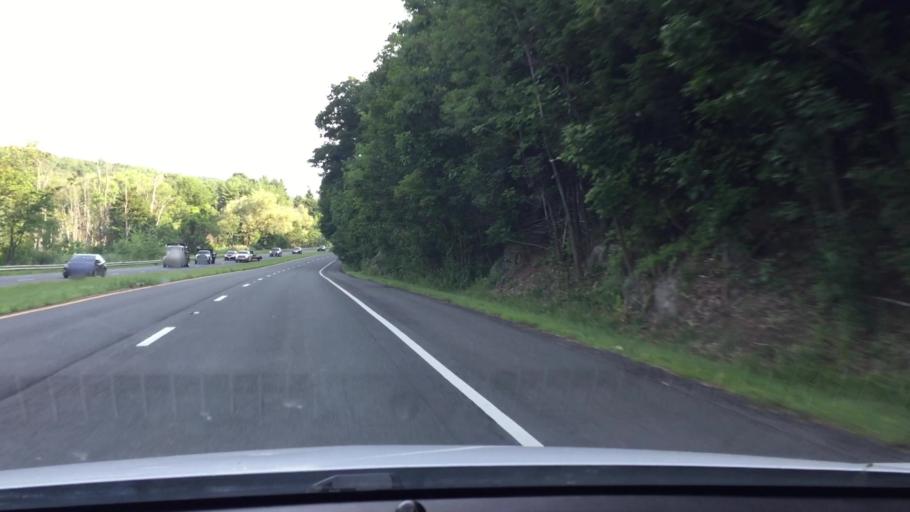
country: US
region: Massachusetts
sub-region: Berkshire County
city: Lenox
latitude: 42.3659
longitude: -73.2763
